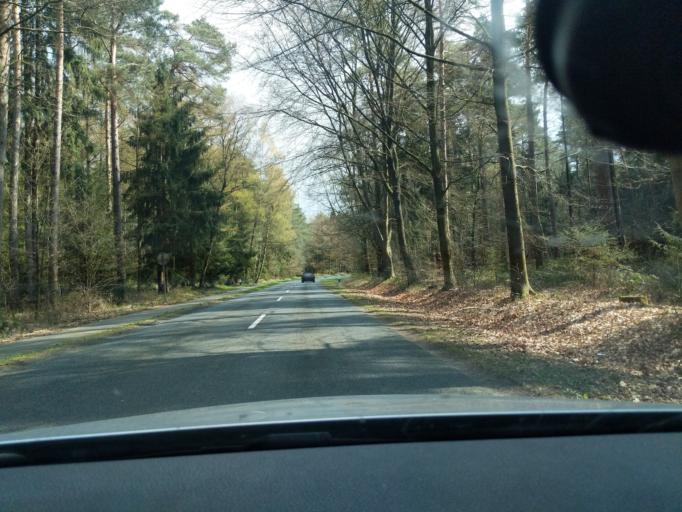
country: DE
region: Lower Saxony
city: Dollern
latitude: 53.5169
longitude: 9.5212
